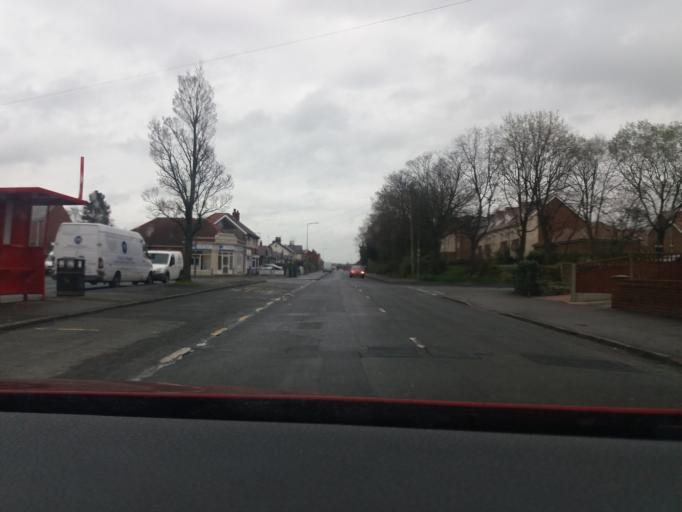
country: GB
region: England
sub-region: Lancashire
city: Chorley
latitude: 53.6426
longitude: -2.6294
